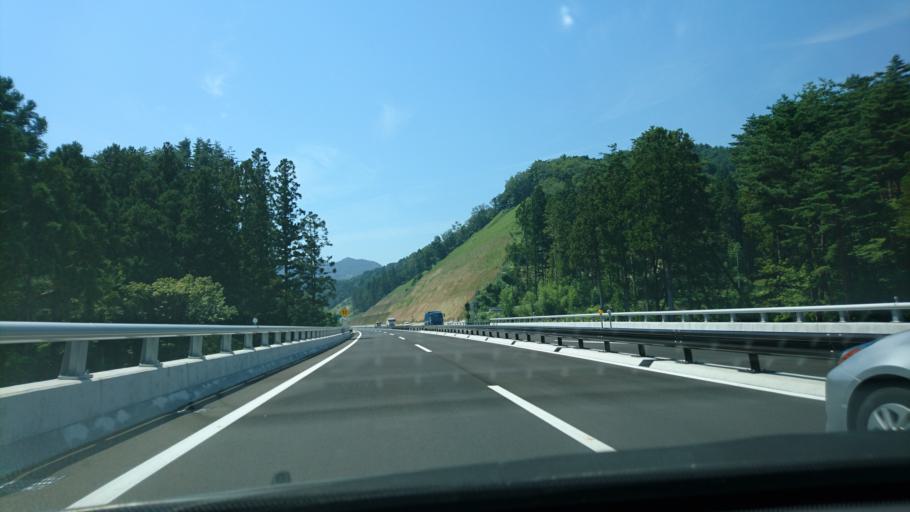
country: JP
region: Iwate
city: Kamaishi
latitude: 39.1547
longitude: 141.8361
